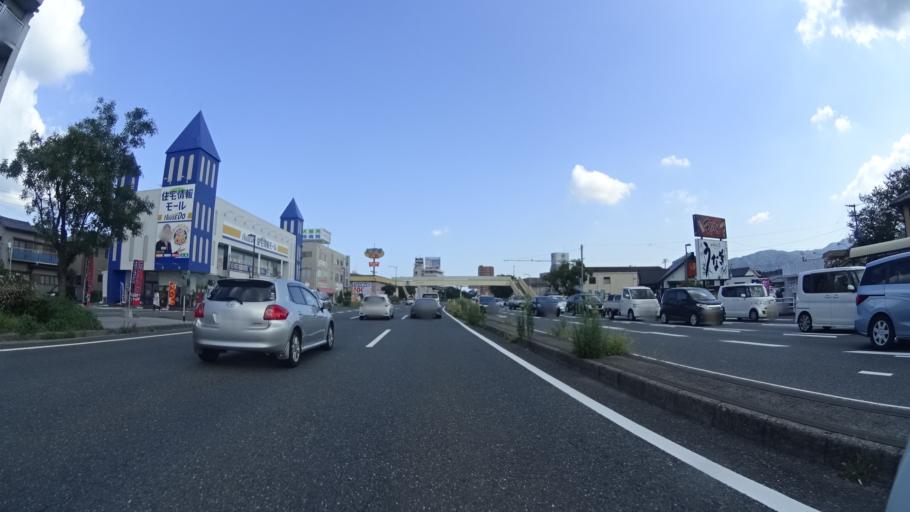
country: JP
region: Fukuoka
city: Kanda
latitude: 33.8302
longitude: 130.9246
